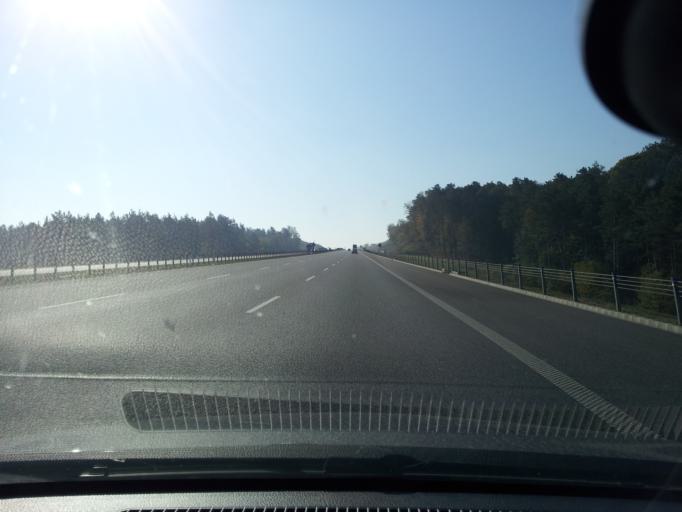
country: PL
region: Kujawsko-Pomorskie
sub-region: Powiat chelminski
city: Lisewo
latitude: 53.3960
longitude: 18.6845
